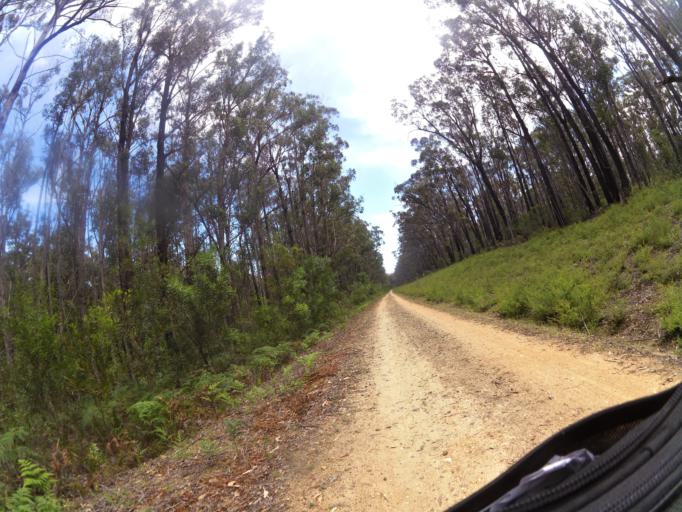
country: AU
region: Victoria
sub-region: East Gippsland
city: Lakes Entrance
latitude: -37.7403
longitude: 148.0132
